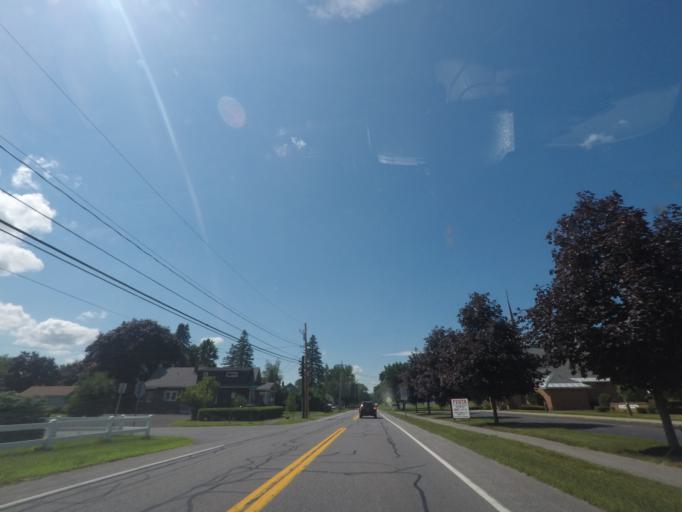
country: US
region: New York
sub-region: Schenectady County
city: Rotterdam
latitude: 42.7939
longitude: -73.9874
